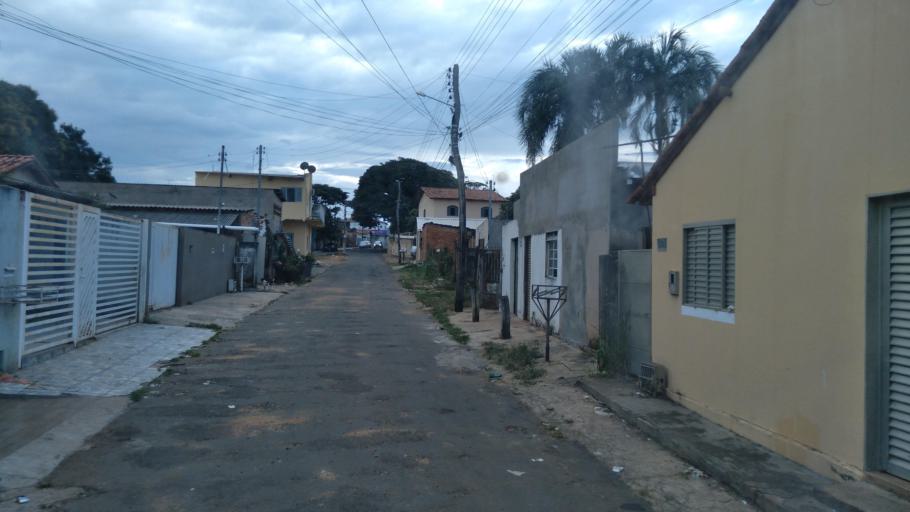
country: BR
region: Goias
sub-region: Mineiros
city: Mineiros
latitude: -17.5701
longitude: -52.5491
